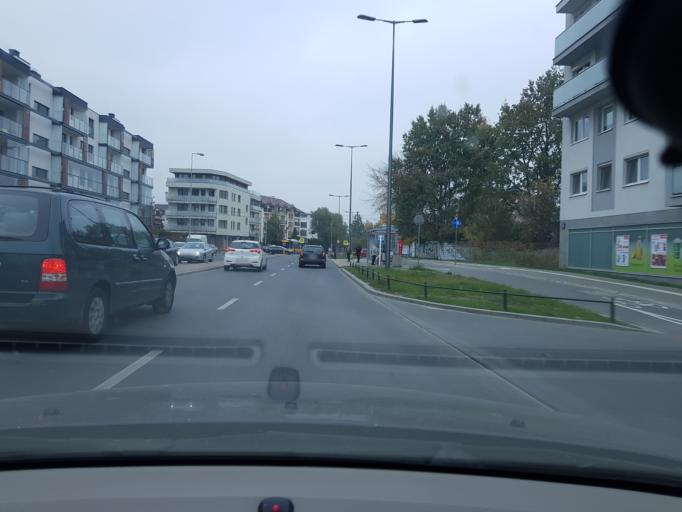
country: PL
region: Masovian Voivodeship
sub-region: Warszawa
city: Ursynow
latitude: 52.1433
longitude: 21.0249
